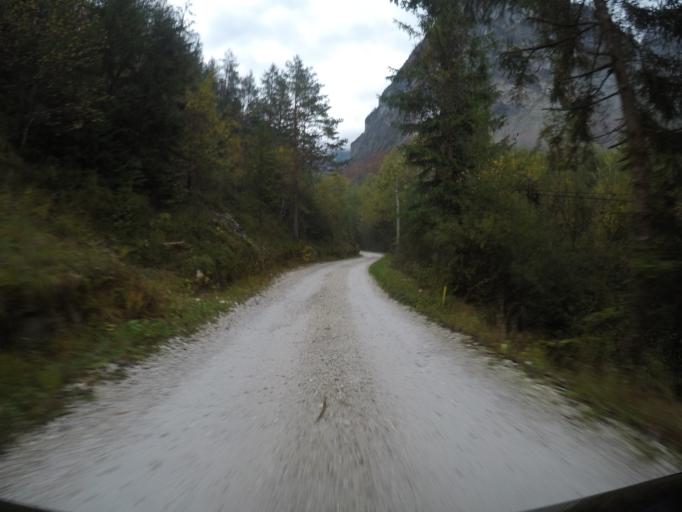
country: SI
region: Kranjska Gora
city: Kranjska Gora
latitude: 46.3824
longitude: 13.7586
